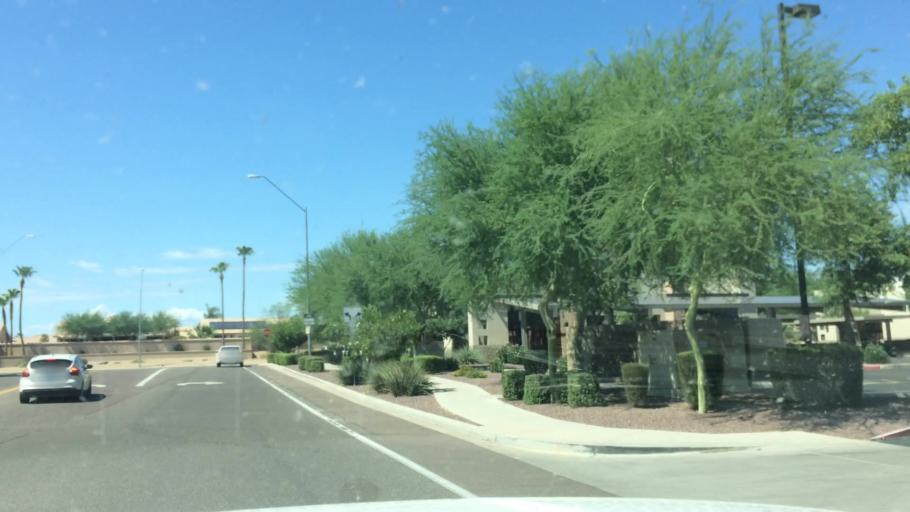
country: US
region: Arizona
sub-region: Maricopa County
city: Sun City
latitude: 33.6518
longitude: -112.2463
